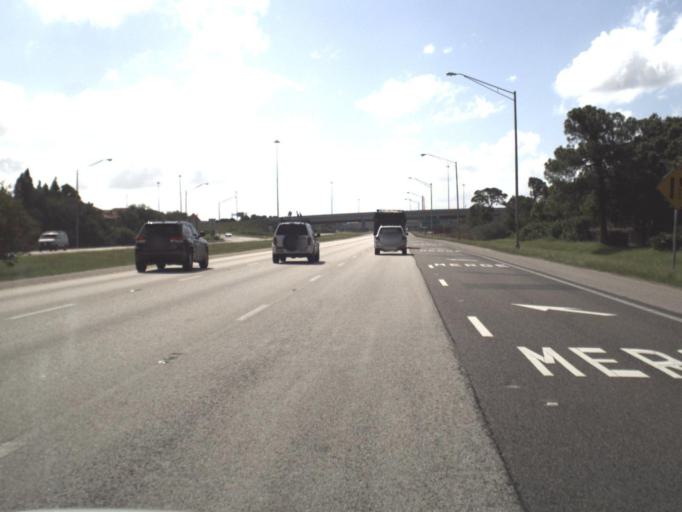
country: US
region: Florida
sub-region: Pinellas County
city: Feather Sound
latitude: 27.8837
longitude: -82.6658
